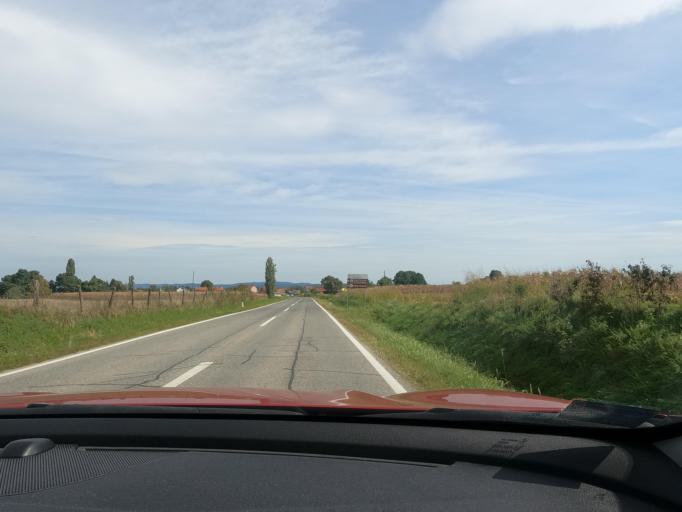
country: HR
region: Sisacko-Moslavacka
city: Osekovo
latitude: 45.5464
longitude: 16.5848
